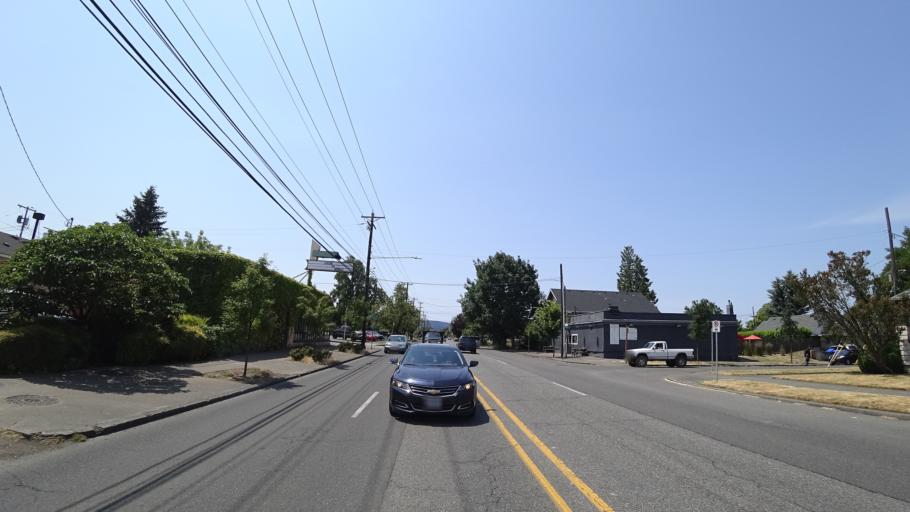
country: US
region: Oregon
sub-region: Multnomah County
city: Portland
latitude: 45.5771
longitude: -122.6899
